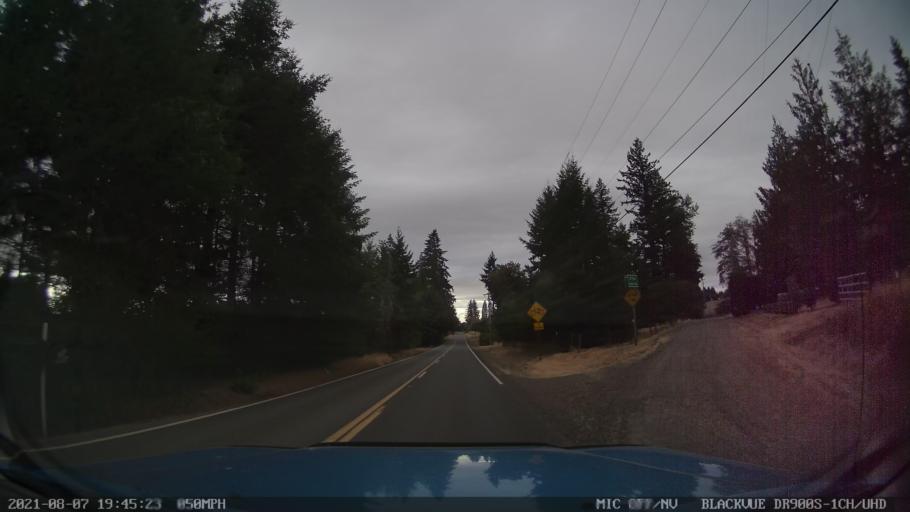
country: US
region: Oregon
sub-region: Marion County
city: Silverton
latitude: 44.9477
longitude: -122.6951
